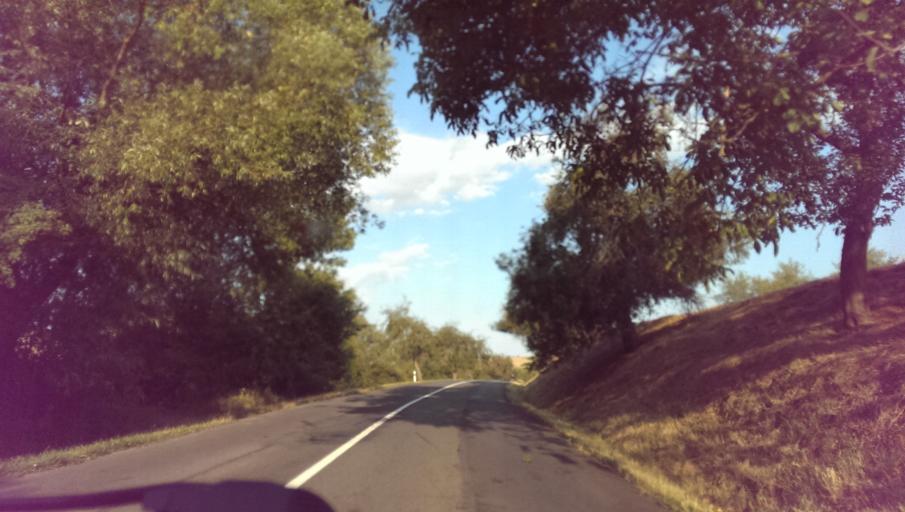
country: CZ
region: Zlin
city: Polesovice
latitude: 49.0510
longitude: 17.2976
